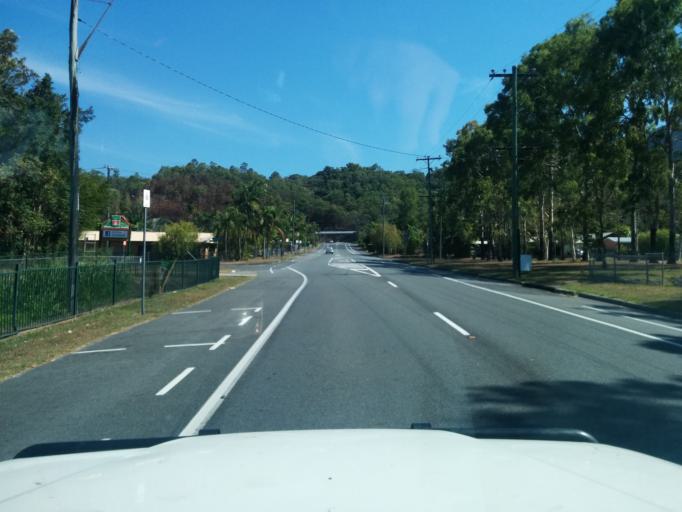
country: AU
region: Queensland
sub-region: Cairns
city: Redlynch
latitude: -16.9114
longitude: 145.7281
